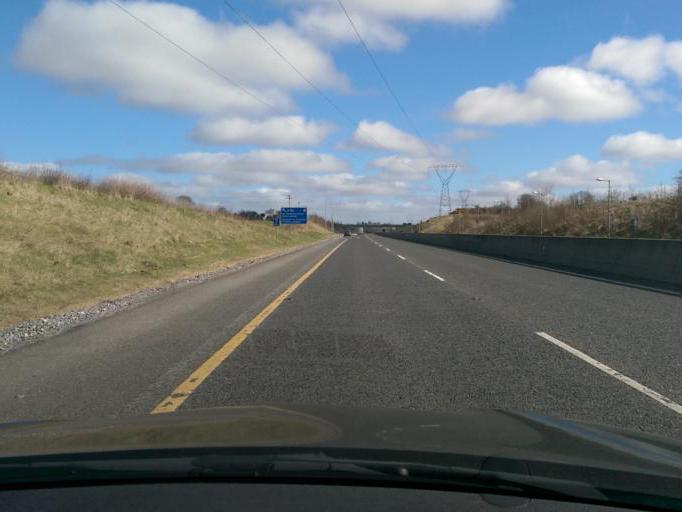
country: IE
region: Leinster
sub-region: An Iarmhi
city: Rochfortbridge
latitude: 53.3844
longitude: -7.3706
